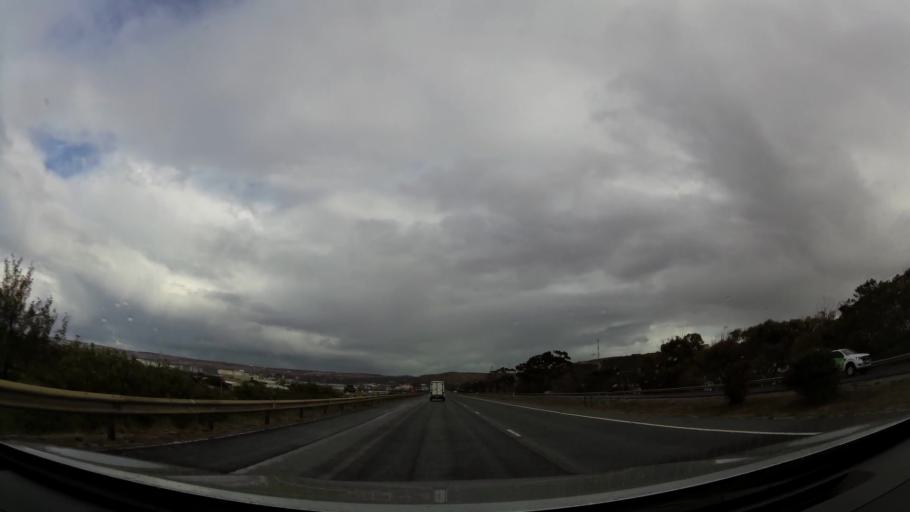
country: ZA
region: Western Cape
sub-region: Eden District Municipality
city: Mossel Bay
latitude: -34.1354
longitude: 22.1017
